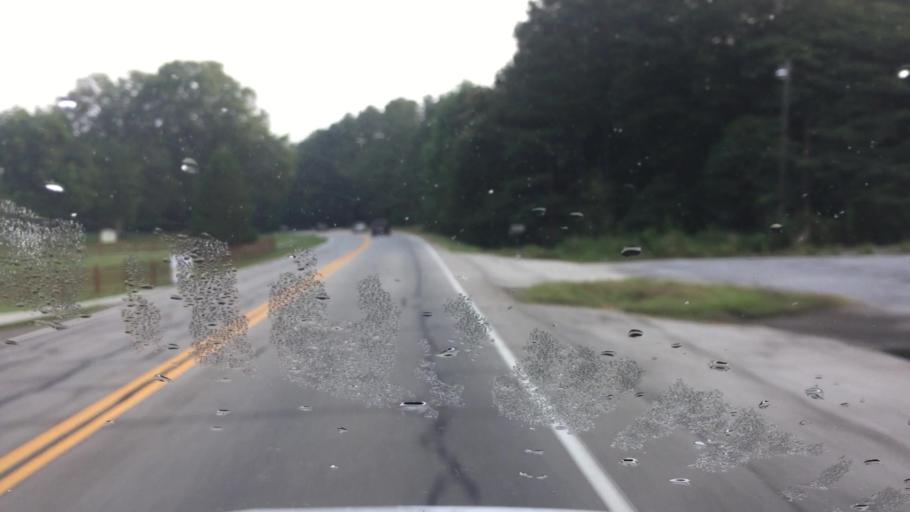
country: US
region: Georgia
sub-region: DeKalb County
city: Pine Mountain
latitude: 33.5958
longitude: -84.1532
